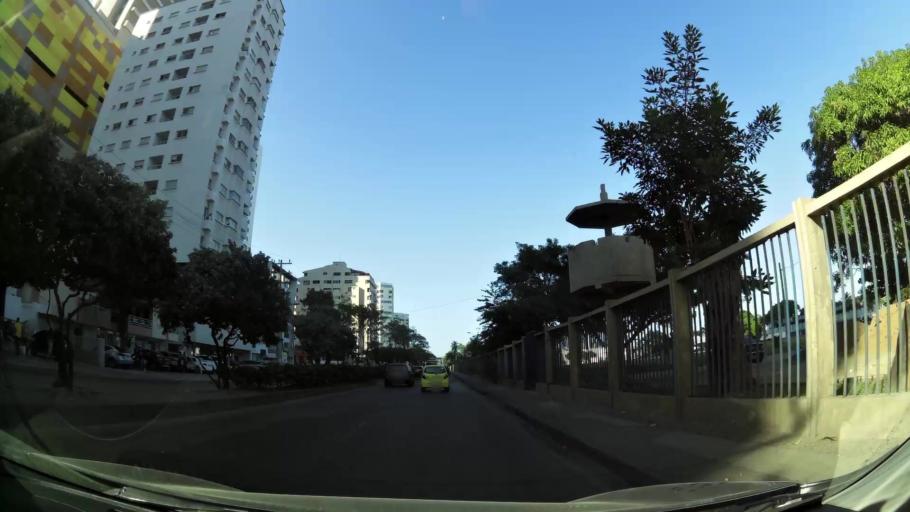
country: CO
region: Bolivar
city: Cartagena
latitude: 10.4106
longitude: -75.5504
